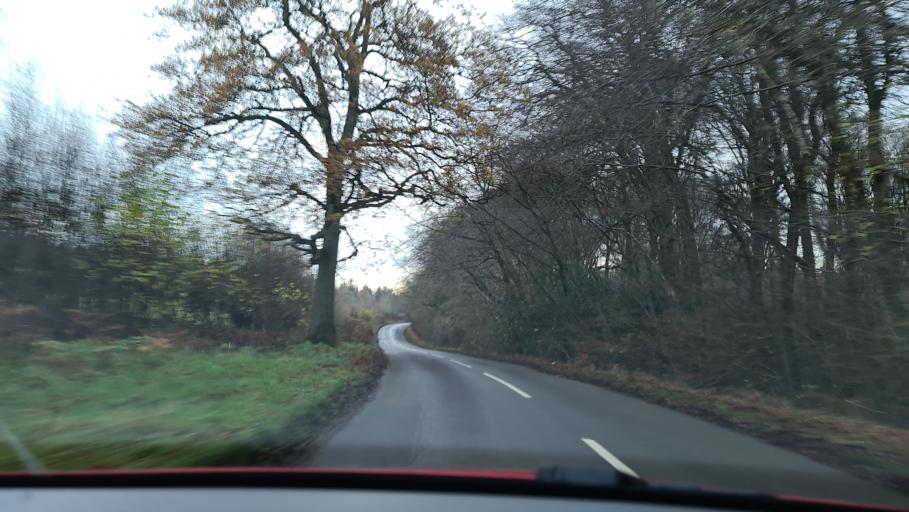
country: GB
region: England
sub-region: Buckinghamshire
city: Princes Risborough
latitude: 51.7093
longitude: -0.7917
